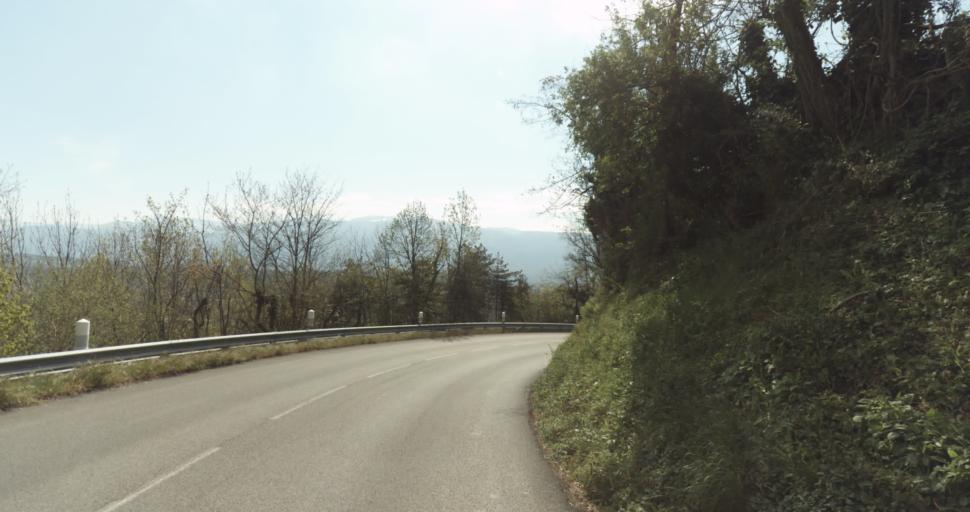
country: FR
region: Rhone-Alpes
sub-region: Departement de l'Isere
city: Saint-Verand
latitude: 45.1688
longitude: 5.3230
